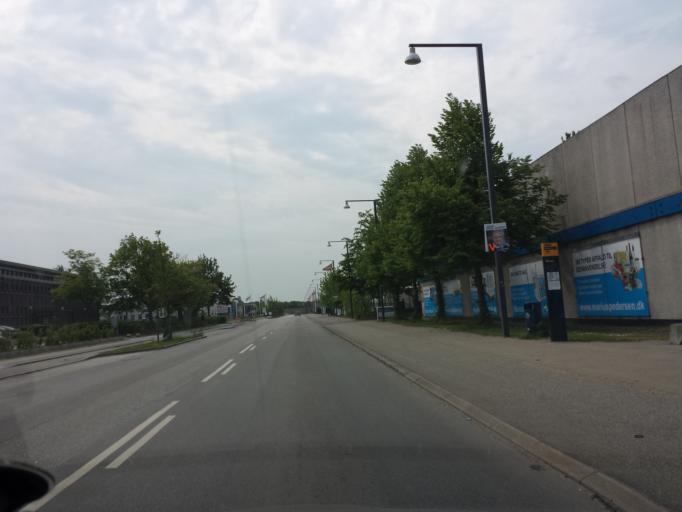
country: DK
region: Capital Region
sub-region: Rodovre Kommune
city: Rodovre
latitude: 55.6966
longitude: 12.4325
